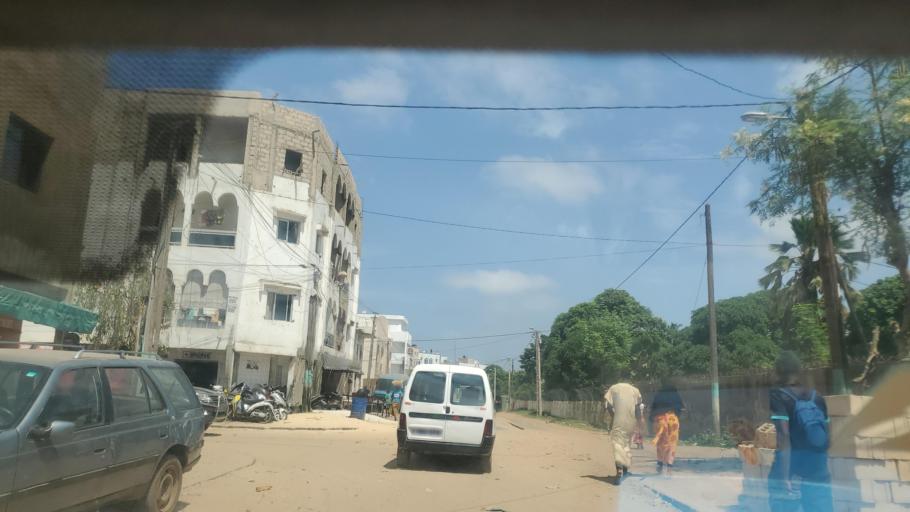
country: SN
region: Dakar
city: Grand Dakar
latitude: 14.7289
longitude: -17.4496
